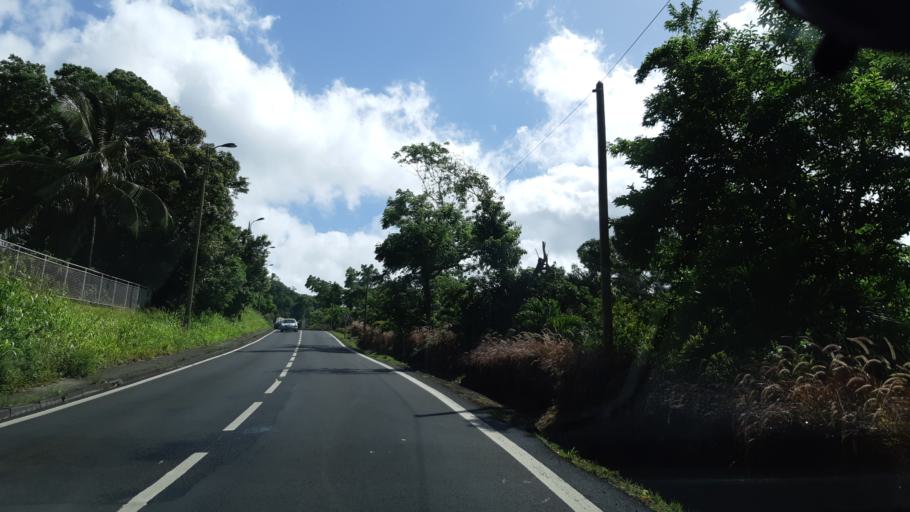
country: GP
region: Guadeloupe
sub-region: Guadeloupe
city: Saint-Claude
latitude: 16.0146
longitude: -61.7089
